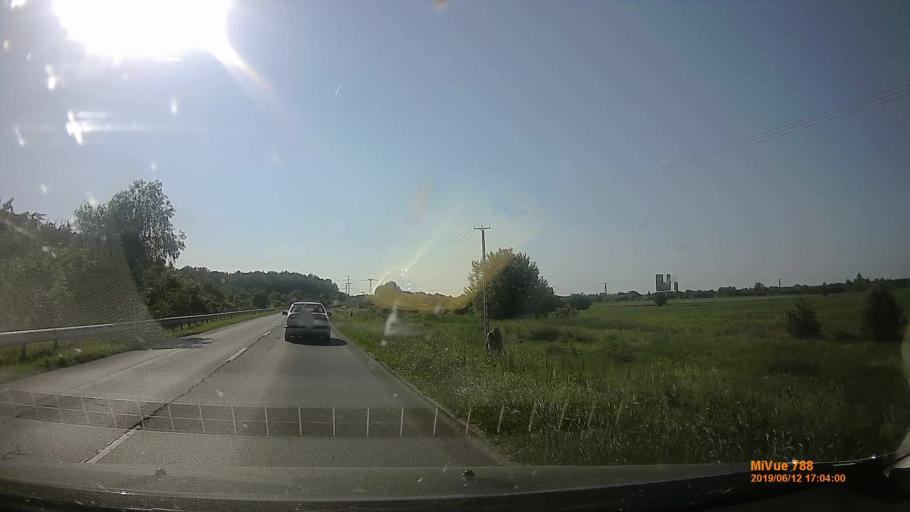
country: HU
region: Csongrad
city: Deszk
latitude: 46.2173
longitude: 20.2091
